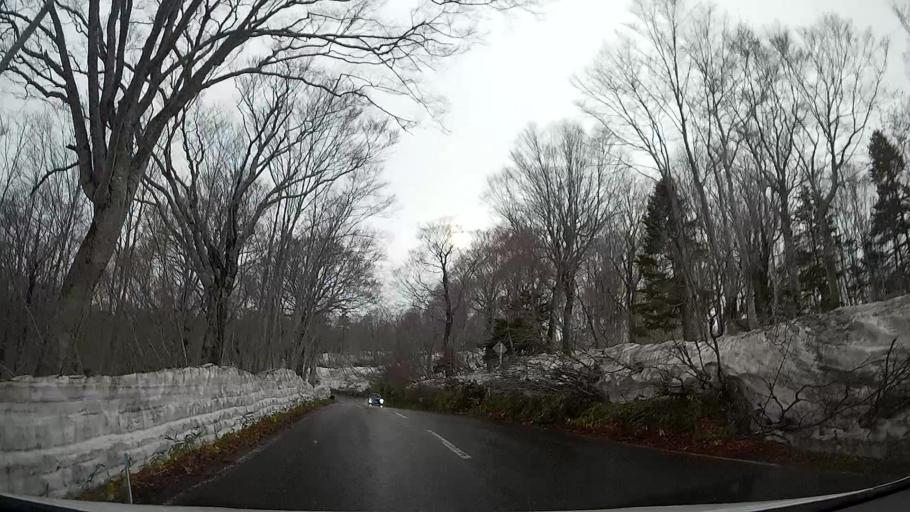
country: JP
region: Aomori
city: Aomori Shi
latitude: 40.6318
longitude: 140.9071
